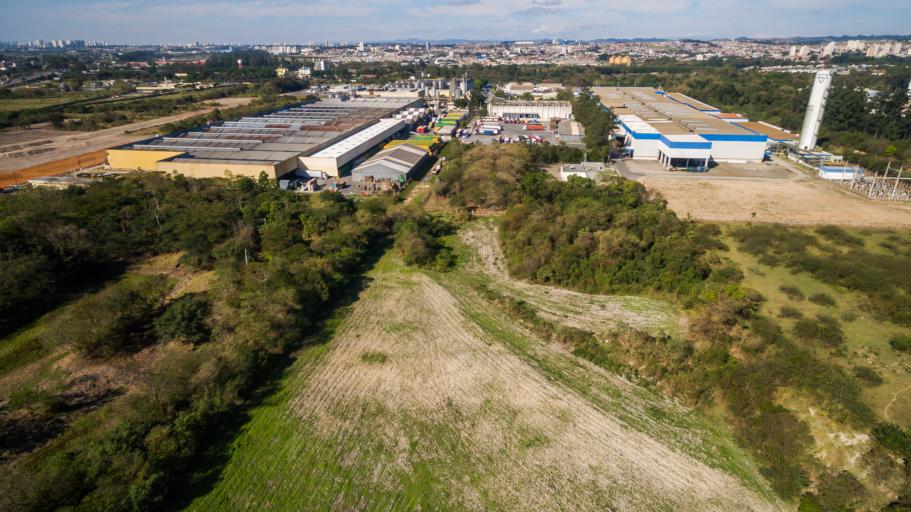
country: BR
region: Sao Paulo
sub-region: Jacarei
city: Jacarei
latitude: -23.2878
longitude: -45.9891
